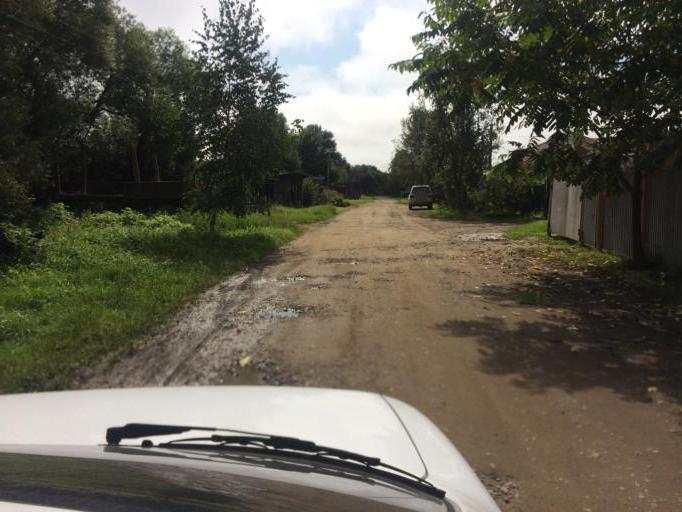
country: RU
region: Primorskiy
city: Dal'nerechensk
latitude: 45.9180
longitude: 133.7242
